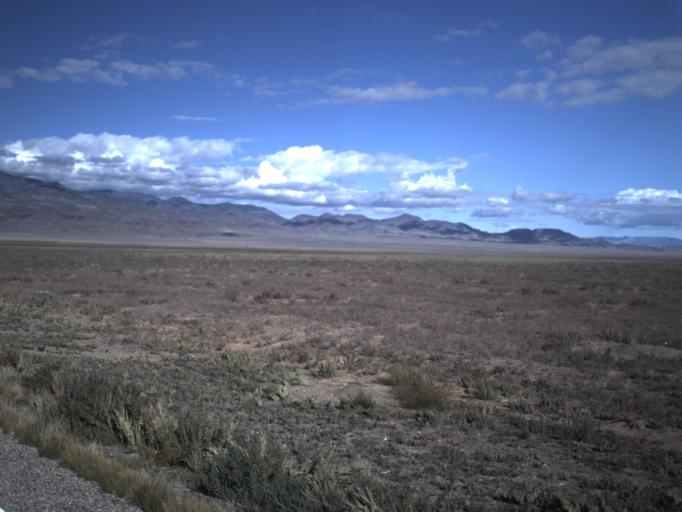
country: US
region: Utah
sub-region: Beaver County
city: Milford
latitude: 38.4618
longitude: -113.3802
